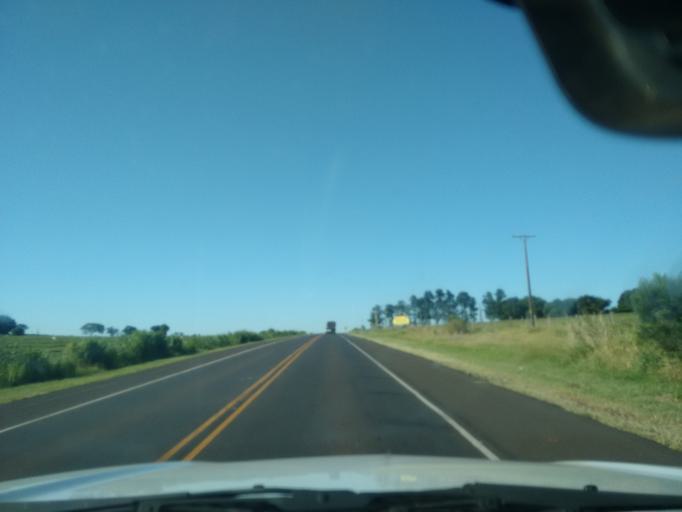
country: PY
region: Canindeyu
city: Salto del Guaira
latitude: -23.9758
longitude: -54.3309
